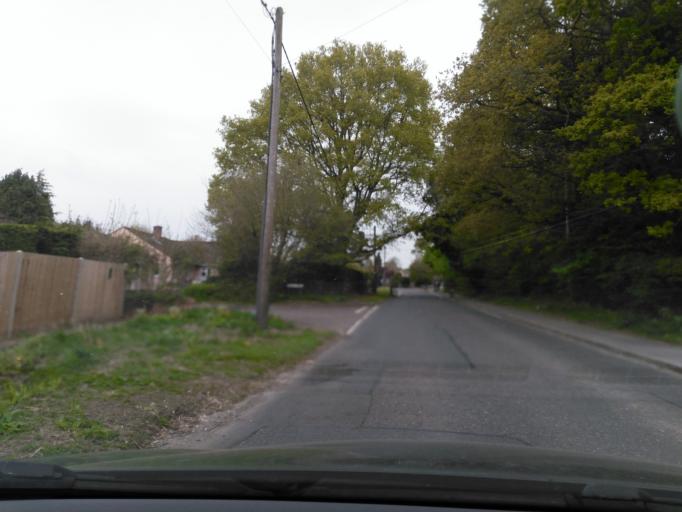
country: GB
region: England
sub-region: West Berkshire
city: Stratfield Mortimer
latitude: 51.3286
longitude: -1.0553
